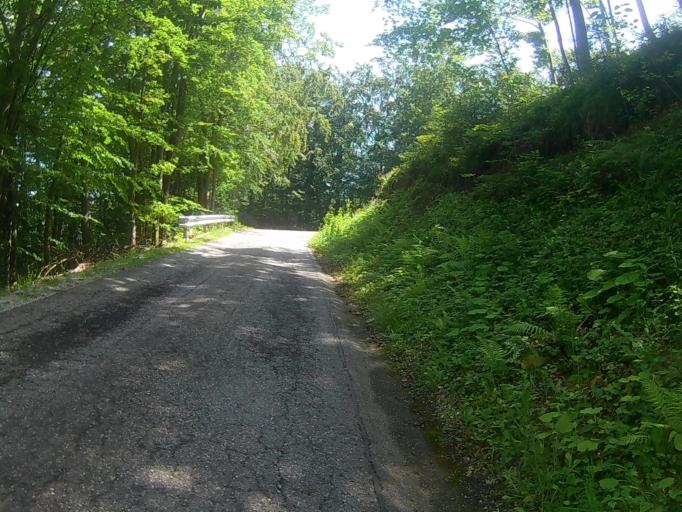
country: SI
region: Maribor
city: Bresternica
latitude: 46.5889
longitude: 15.5521
